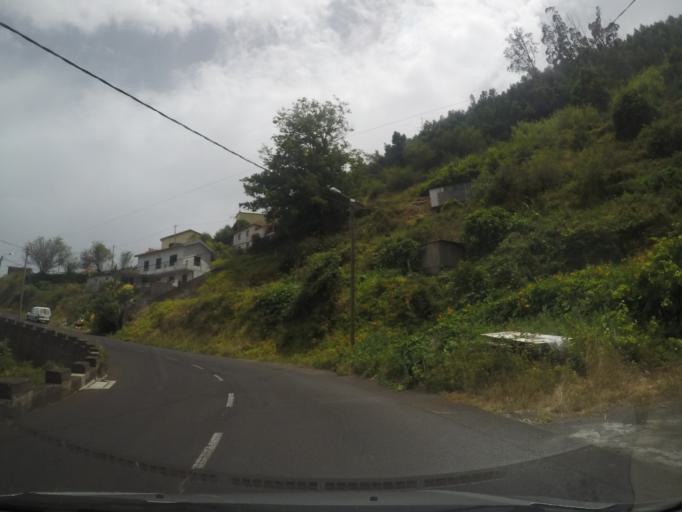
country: PT
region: Madeira
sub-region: Santa Cruz
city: Camacha
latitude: 32.6710
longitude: -16.8409
